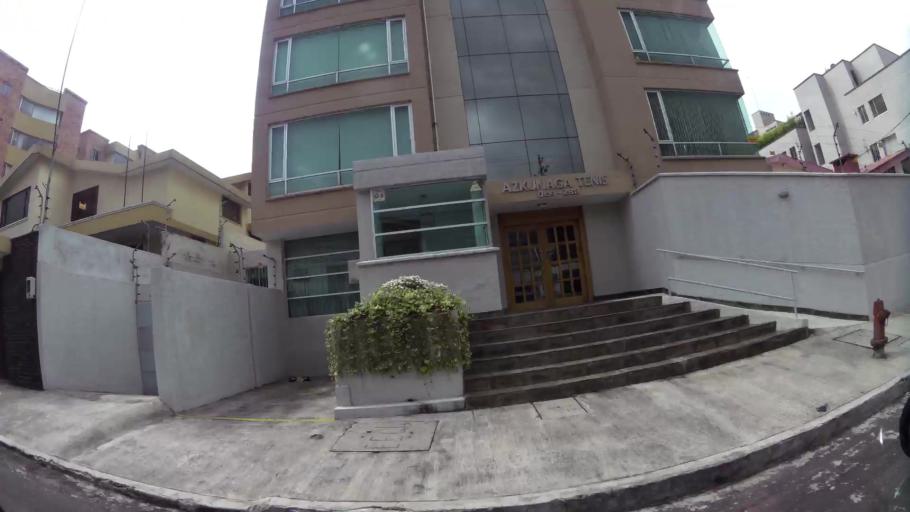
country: EC
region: Pichincha
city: Quito
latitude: -0.1686
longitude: -78.4927
